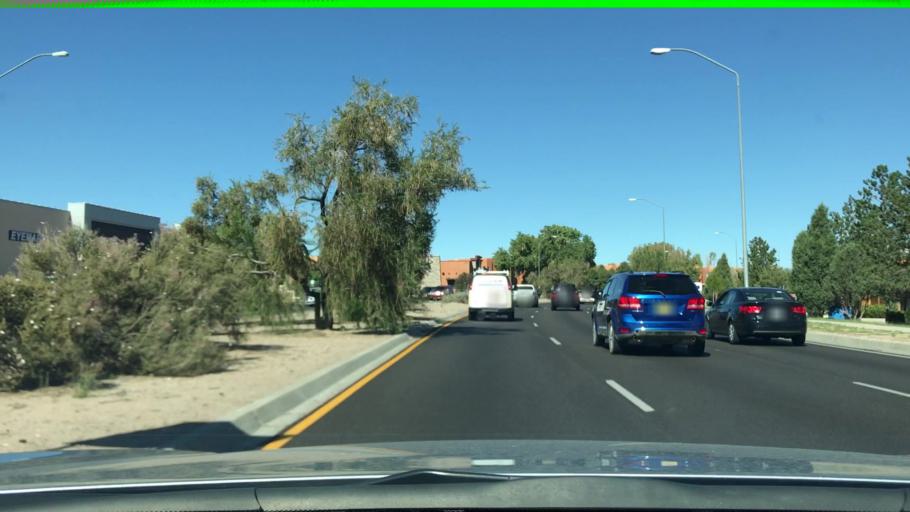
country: US
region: New Mexico
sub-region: Sandoval County
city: Rio Rancho
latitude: 35.1964
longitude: -106.6593
